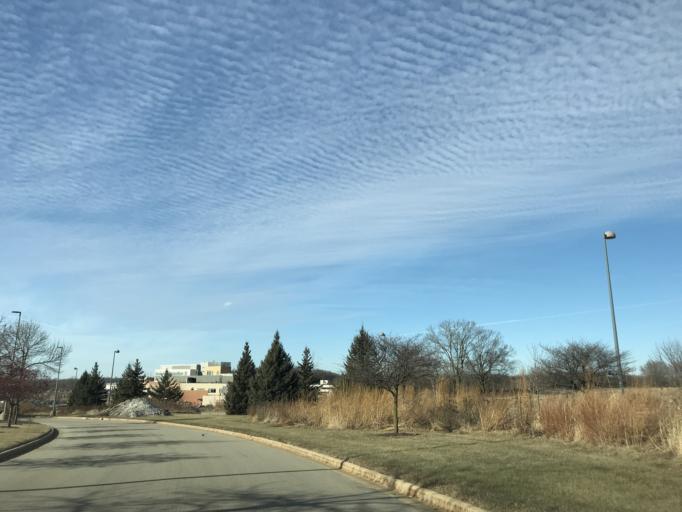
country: US
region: Wisconsin
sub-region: Dane County
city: Windsor
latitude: 43.1516
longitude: -89.2946
